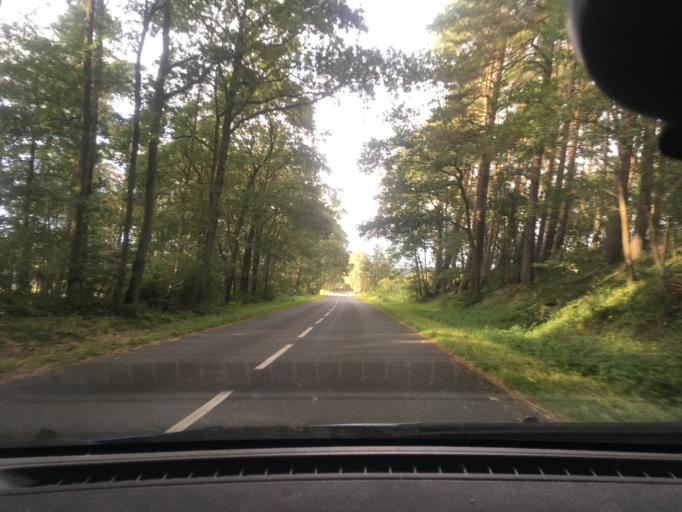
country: DE
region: Lower Saxony
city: Gohrde
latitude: 53.1552
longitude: 10.8677
